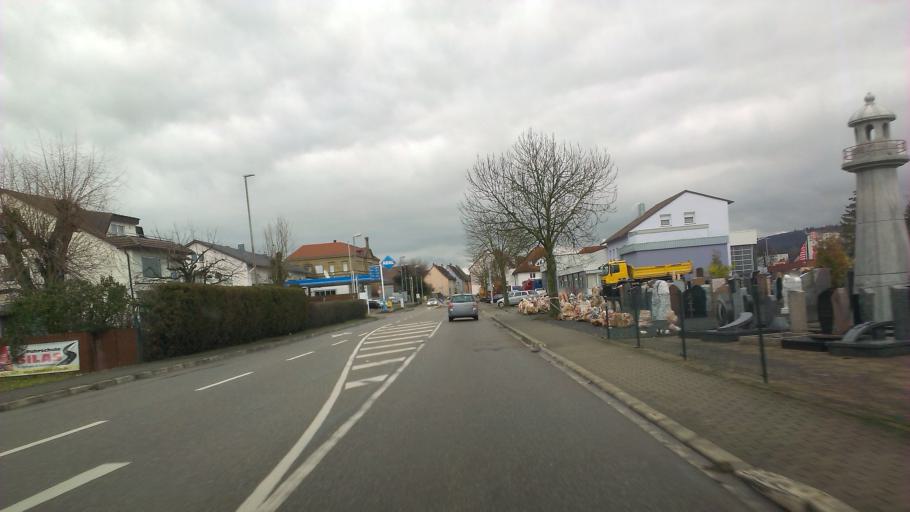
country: DE
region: Baden-Wuerttemberg
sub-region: Regierungsbezirk Stuttgart
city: Eppingen
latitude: 49.1346
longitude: 8.8999
